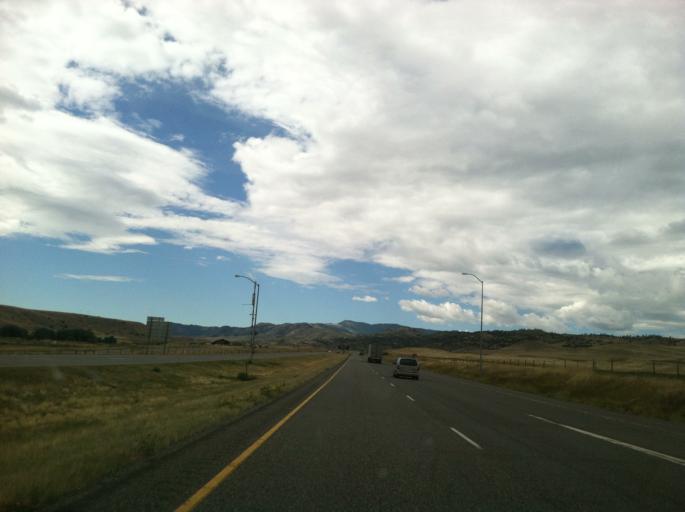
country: US
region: Montana
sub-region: Park County
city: Livingston
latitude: 45.6530
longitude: -110.6171
